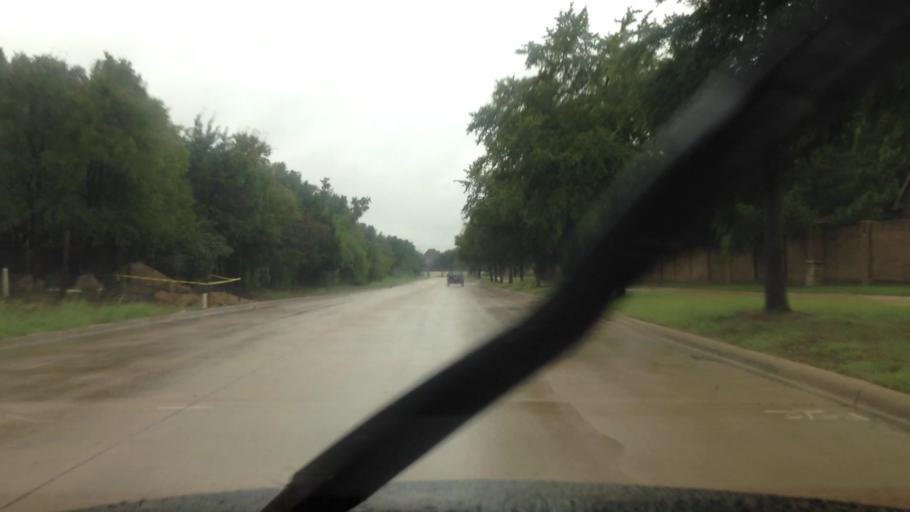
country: US
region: Texas
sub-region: Tarrant County
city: Keller
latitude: 32.9110
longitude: -97.2107
